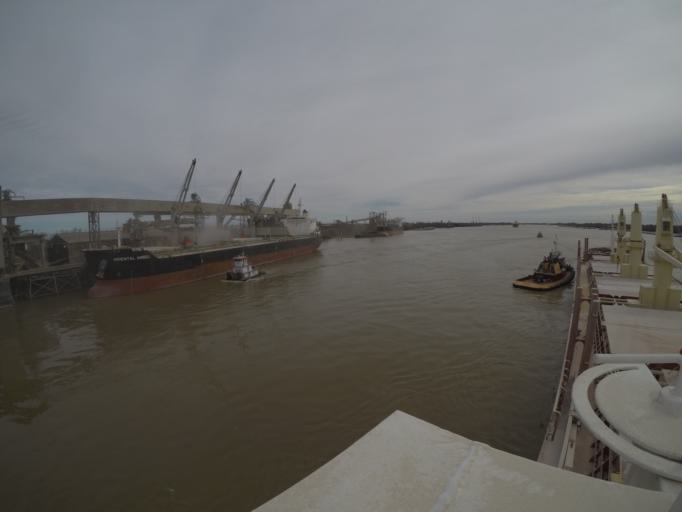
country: US
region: Louisiana
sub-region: Saint John the Baptist Parish
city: Edgard
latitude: 30.0522
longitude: -90.5789
